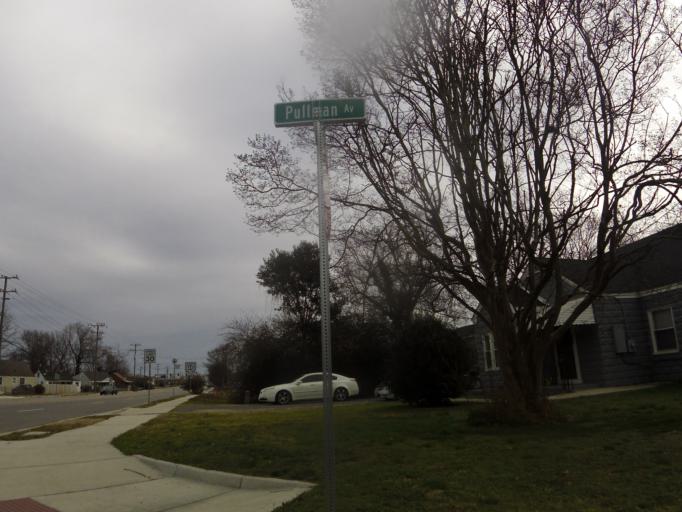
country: US
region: Virginia
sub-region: City of Portsmouth
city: Portsmouth Heights
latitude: 36.8237
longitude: -76.3410
